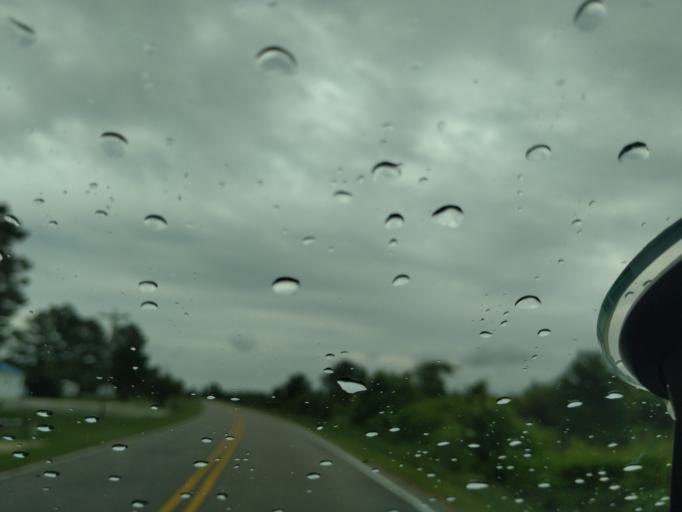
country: US
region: North Carolina
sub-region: Beaufort County
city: Belhaven
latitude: 35.7559
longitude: -76.5160
